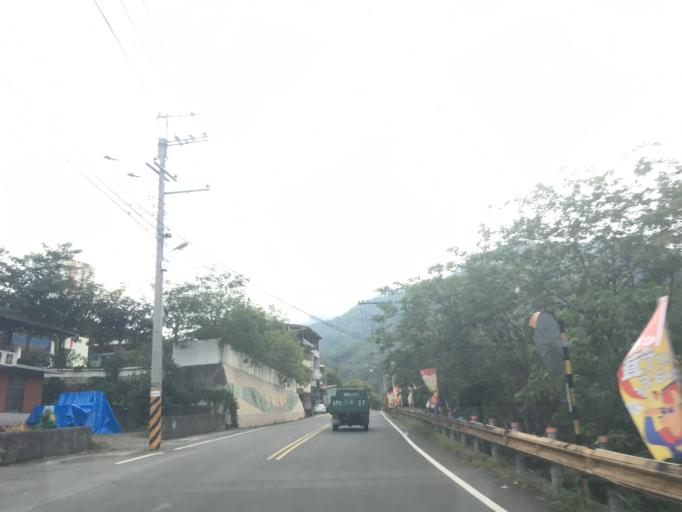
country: TW
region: Taiwan
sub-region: Nantou
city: Puli
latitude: 23.9512
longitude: 120.8694
